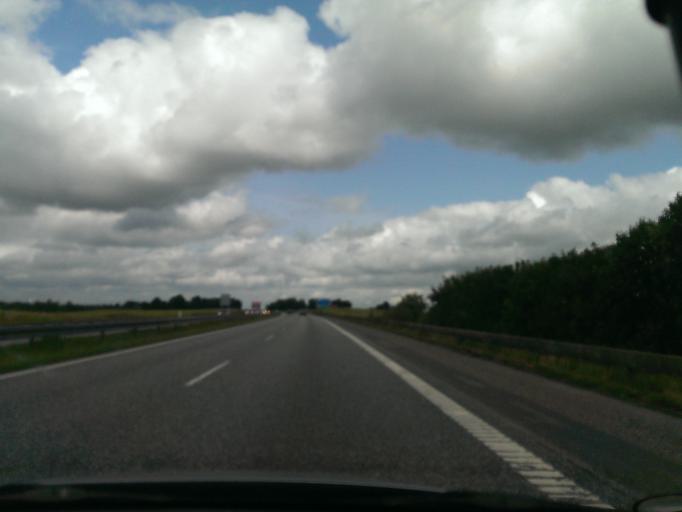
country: DK
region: North Denmark
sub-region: Mariagerfjord Kommune
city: Hobro
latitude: 56.5755
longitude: 9.8399
